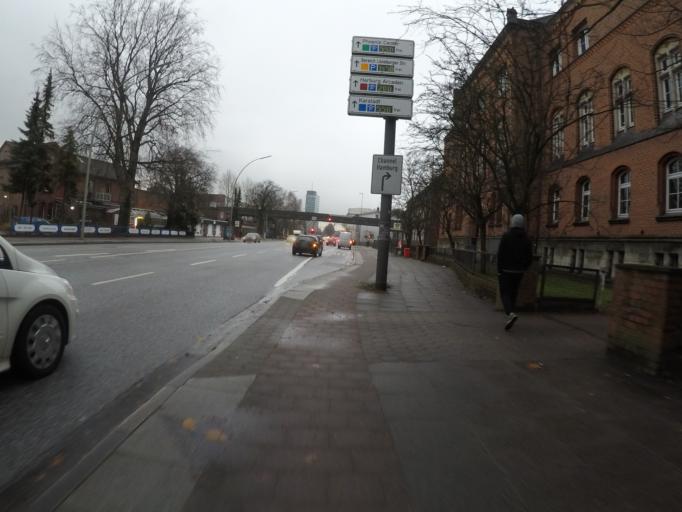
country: DE
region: Hamburg
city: Harburg
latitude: 53.4651
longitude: 9.9768
